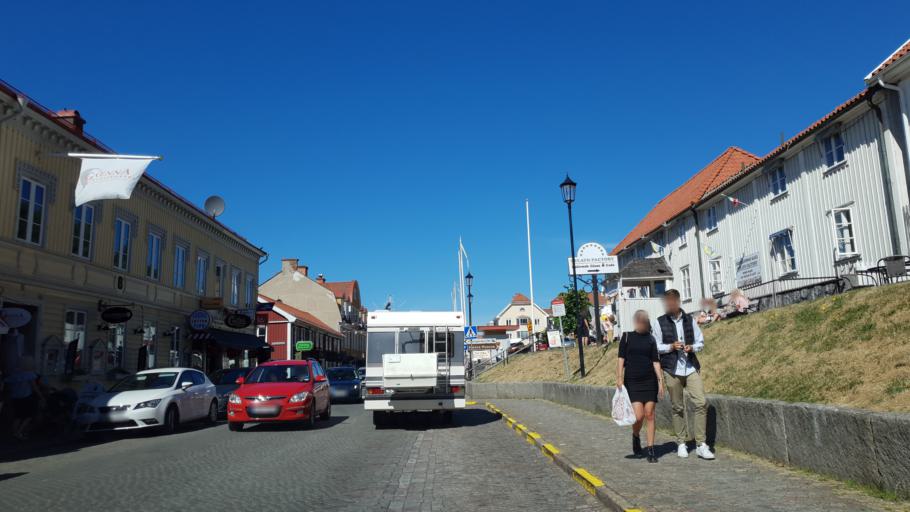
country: SE
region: Joenkoeping
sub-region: Jonkopings Kommun
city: Graenna
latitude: 58.0221
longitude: 14.4667
